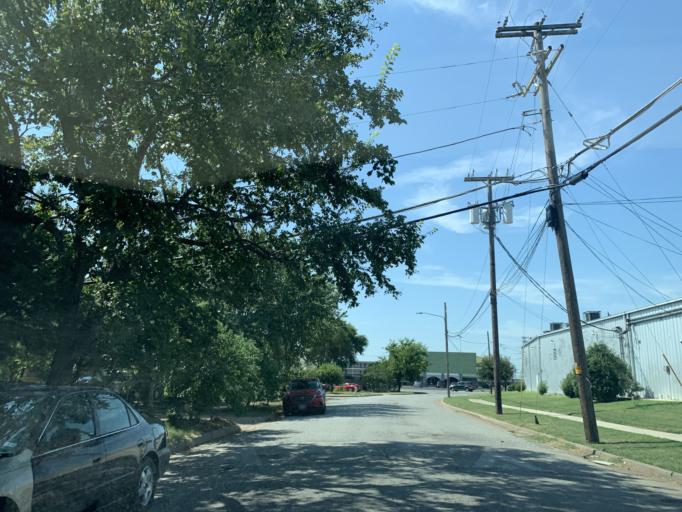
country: US
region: Texas
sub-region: Tarrant County
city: Edgecliff Village
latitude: 32.6775
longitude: -97.3190
